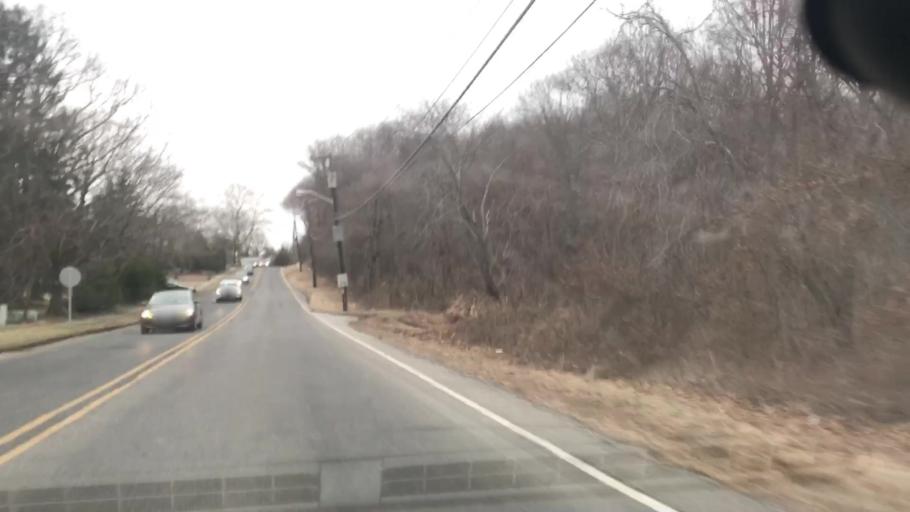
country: US
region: New Jersey
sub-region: Monmouth County
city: Fairview
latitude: 40.3722
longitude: -74.0996
